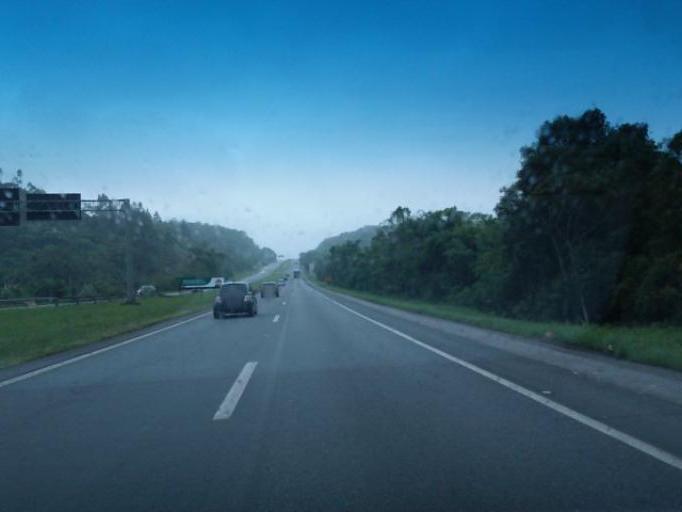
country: BR
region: Parana
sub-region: Campina Grande Do Sul
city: Campina Grande do Sul
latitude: -25.2793
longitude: -48.9259
